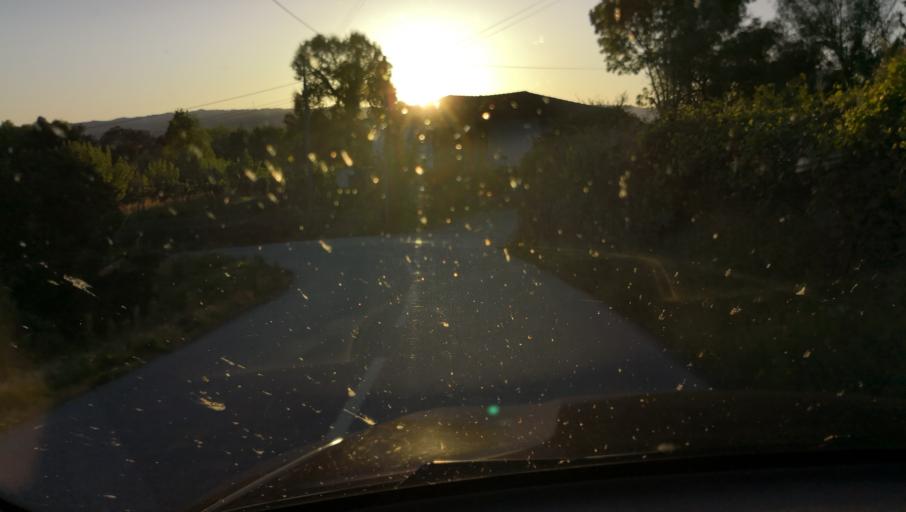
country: PT
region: Vila Real
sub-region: Mondim de Basto
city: Mondim de Basto
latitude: 41.4100
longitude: -7.9474
